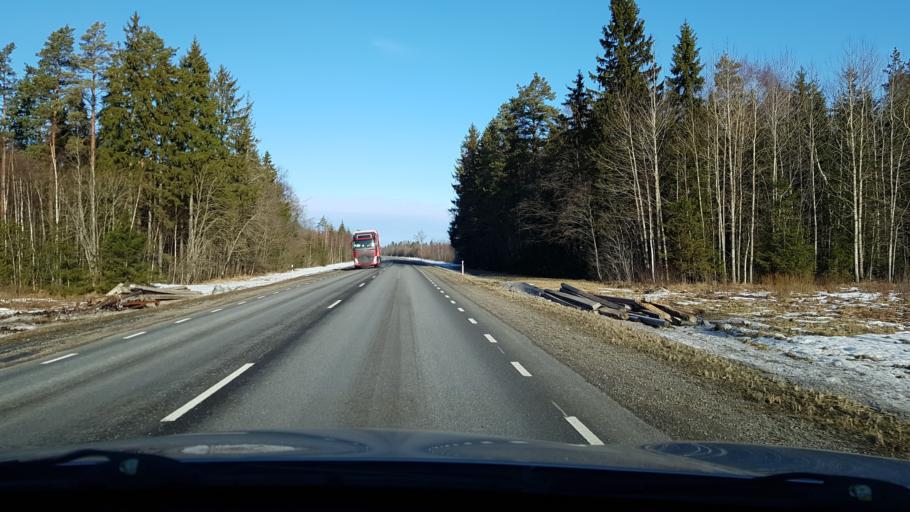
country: EE
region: Viljandimaa
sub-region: Vohma linn
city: Vohma
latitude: 58.6103
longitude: 25.5718
